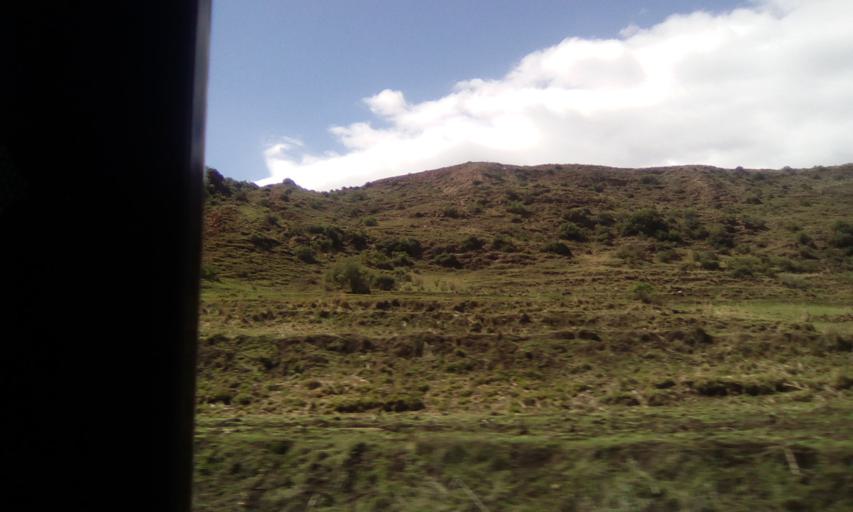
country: LS
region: Maseru
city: Nako
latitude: -29.6555
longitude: 27.8171
